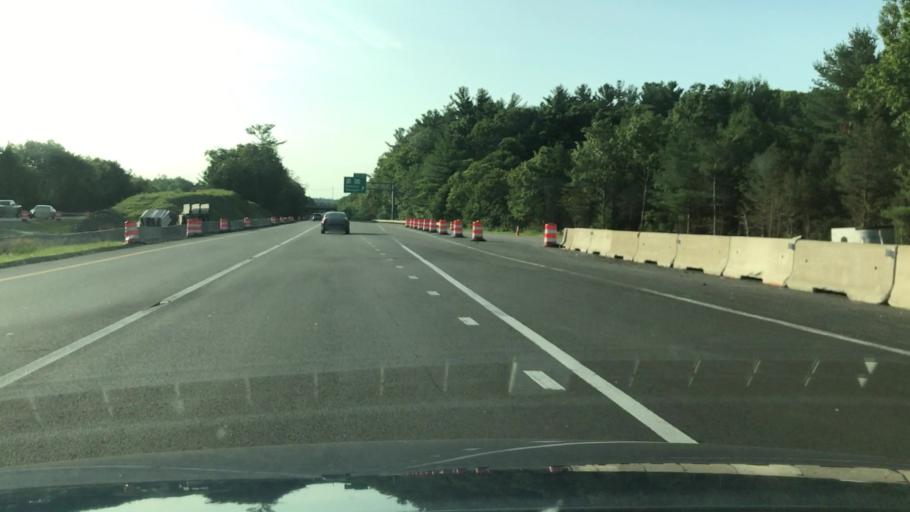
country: US
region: Massachusetts
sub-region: Plymouth County
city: Hanover
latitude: 42.1534
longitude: -70.8512
